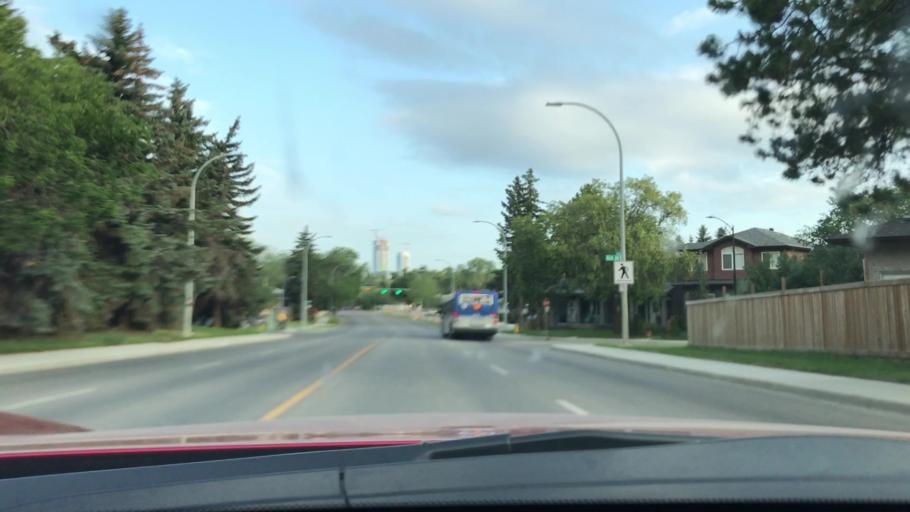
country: CA
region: Alberta
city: Edmonton
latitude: 53.5272
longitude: -113.4624
